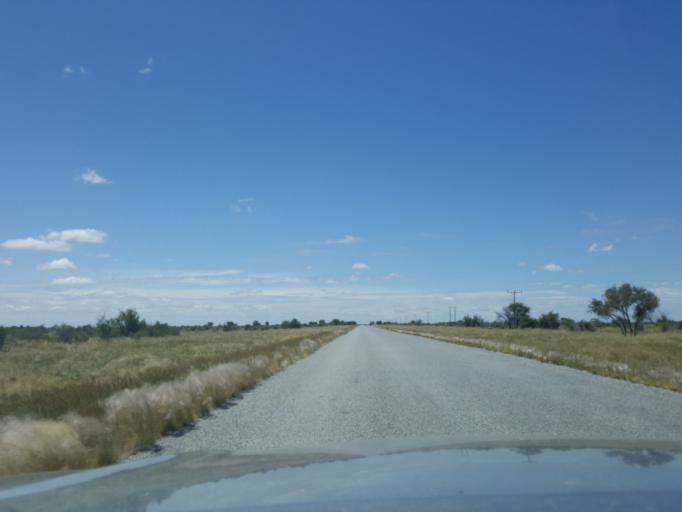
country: BW
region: Central
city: Nata
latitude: -20.1966
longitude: 26.0999
